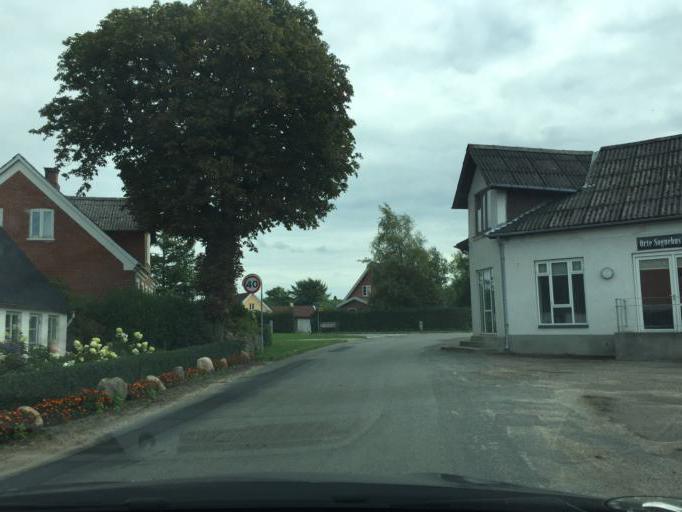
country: DK
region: South Denmark
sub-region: Assens Kommune
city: Arup
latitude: 55.3486
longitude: 10.0932
